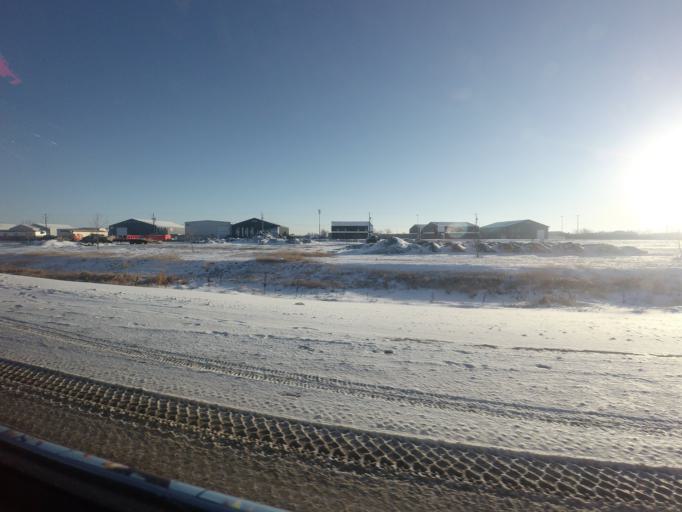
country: CA
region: Saskatchewan
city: Saskatoon
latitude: 52.1676
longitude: -106.6875
